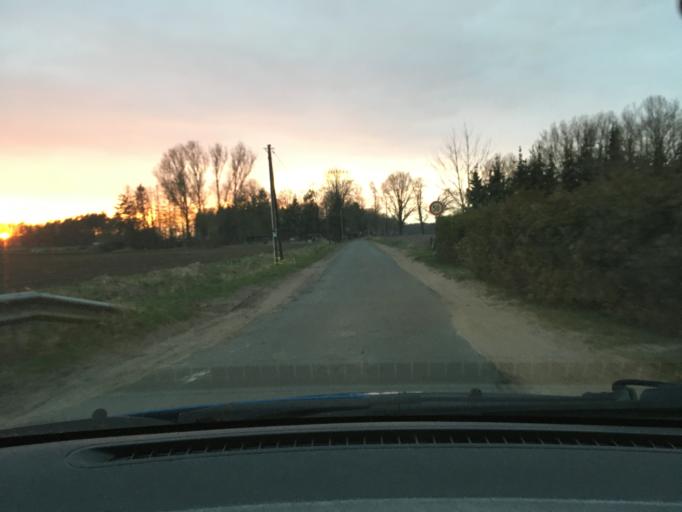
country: DE
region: Lower Saxony
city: Bleckede
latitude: 53.2996
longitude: 10.6728
